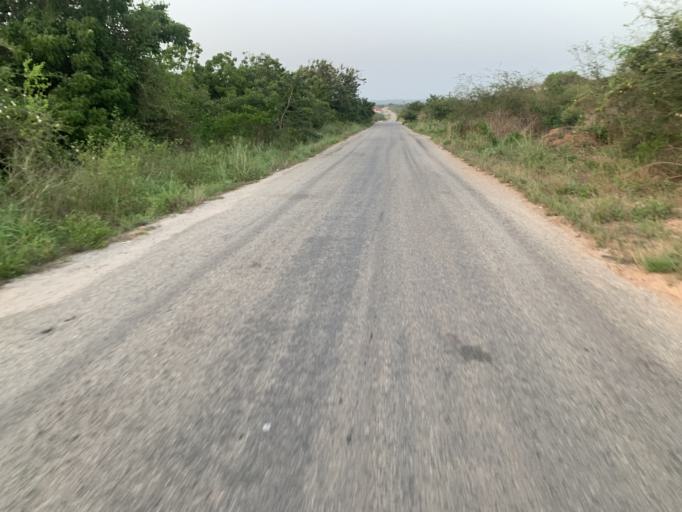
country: GH
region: Central
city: Winneba
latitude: 5.3710
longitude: -0.6160
